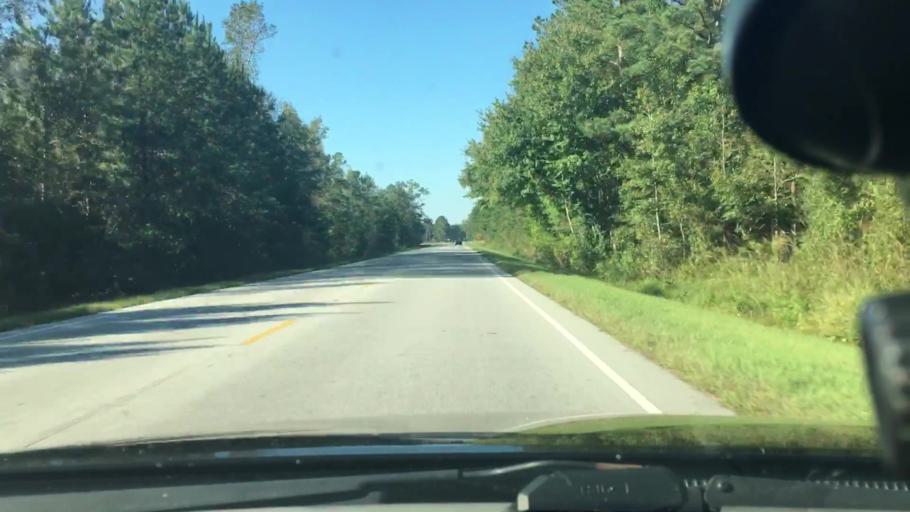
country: US
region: North Carolina
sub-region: Craven County
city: Vanceboro
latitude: 35.3237
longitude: -77.1467
